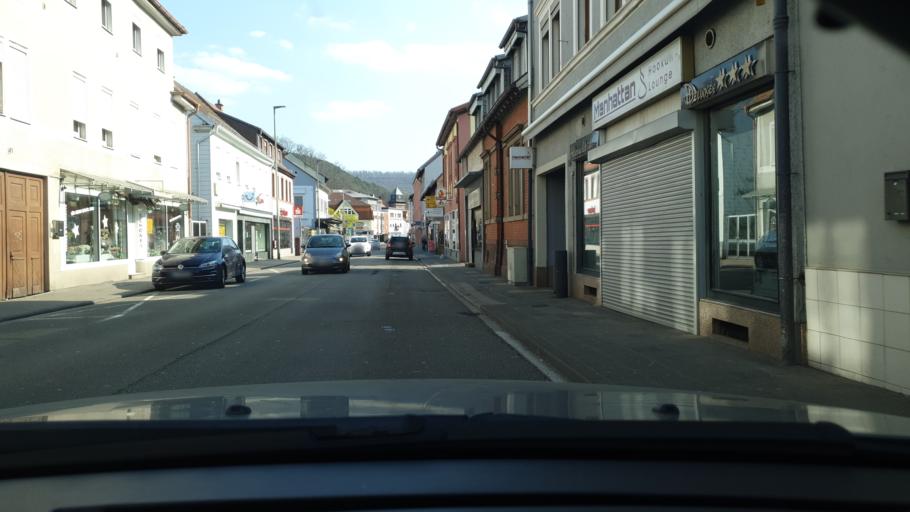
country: DE
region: Rheinland-Pfalz
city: Landstuhl
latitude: 49.4137
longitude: 7.5671
